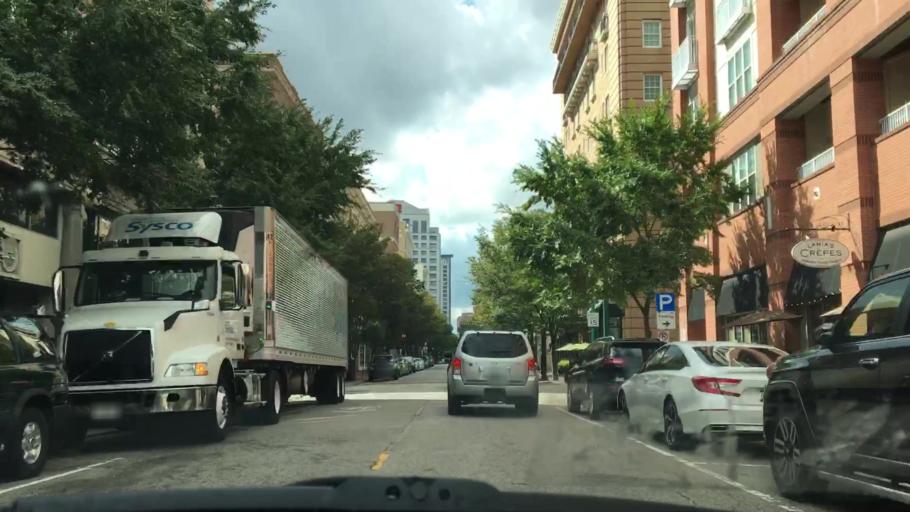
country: US
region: Virginia
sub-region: City of Norfolk
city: Norfolk
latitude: 36.8516
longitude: -76.2897
